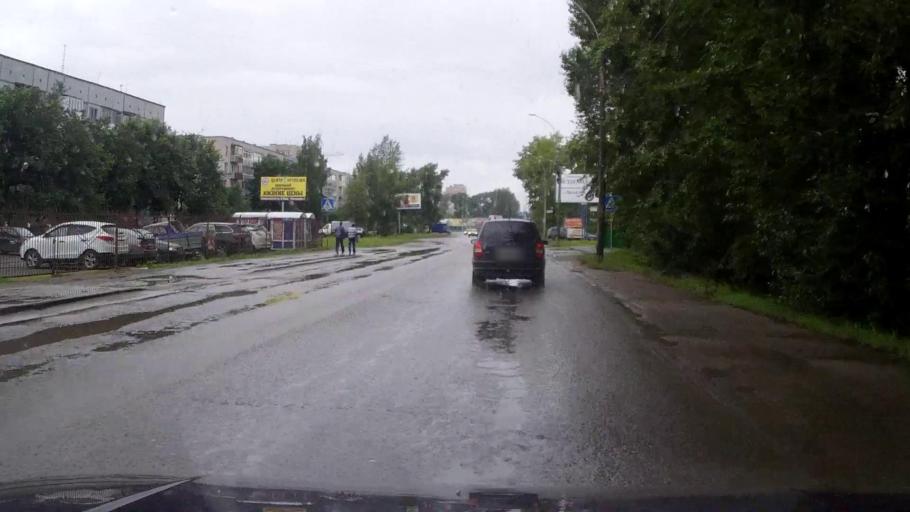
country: RU
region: Vologda
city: Vologda
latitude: 59.2101
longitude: 39.8561
